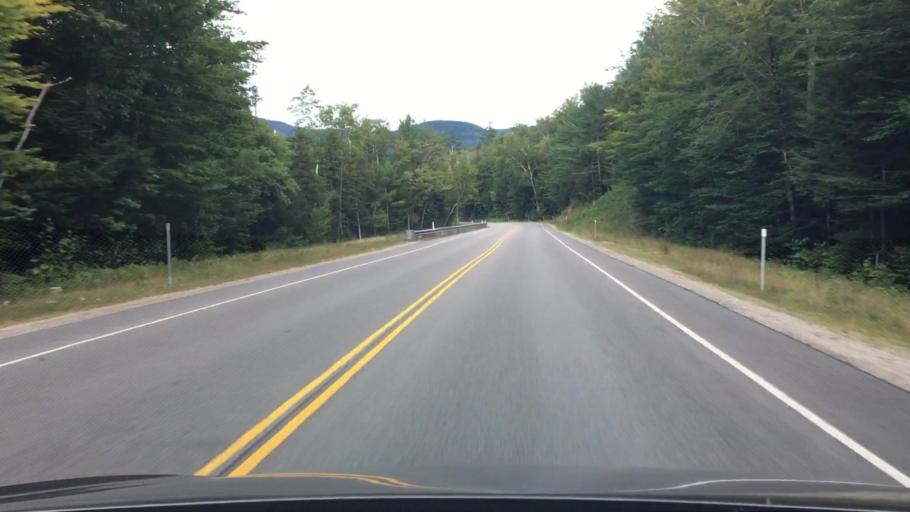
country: US
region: New Hampshire
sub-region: Carroll County
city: Tamworth
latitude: 44.0077
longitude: -71.2740
